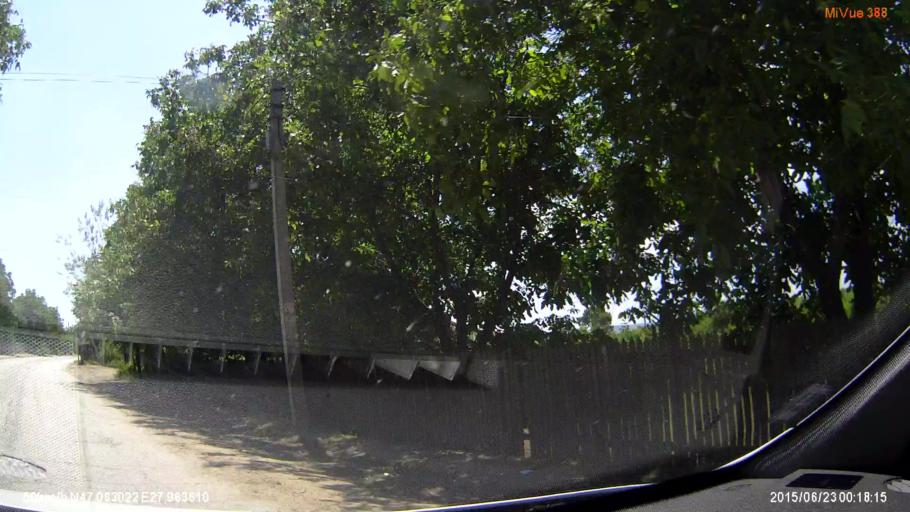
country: RO
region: Iasi
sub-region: Comuna Prisacani
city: Prisacani
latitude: 47.0631
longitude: 27.9635
